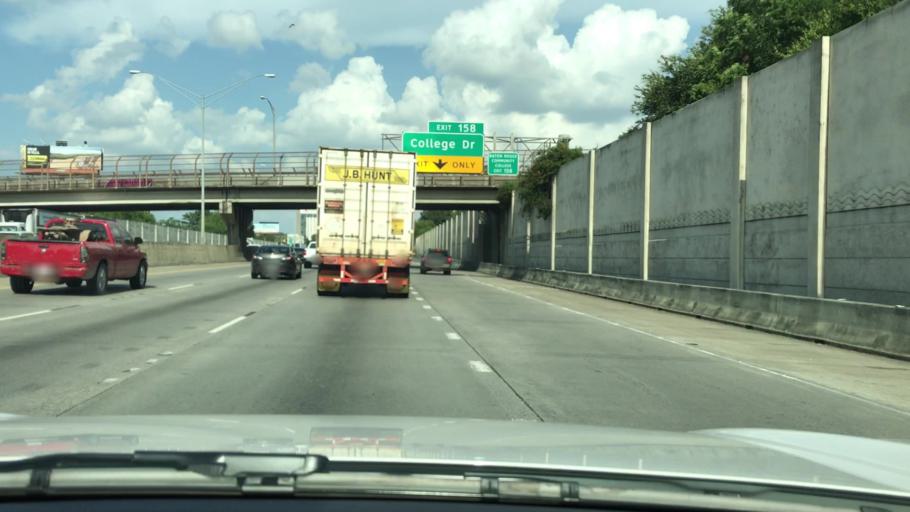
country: US
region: Louisiana
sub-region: East Baton Rouge Parish
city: Baton Rouge
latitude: 30.4236
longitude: -91.1467
